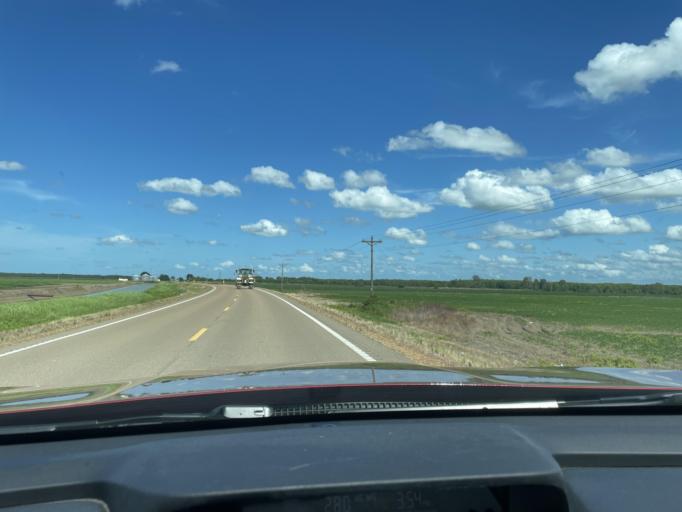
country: US
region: Mississippi
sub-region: Humphreys County
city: Belzoni
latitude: 33.1832
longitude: -90.6575
